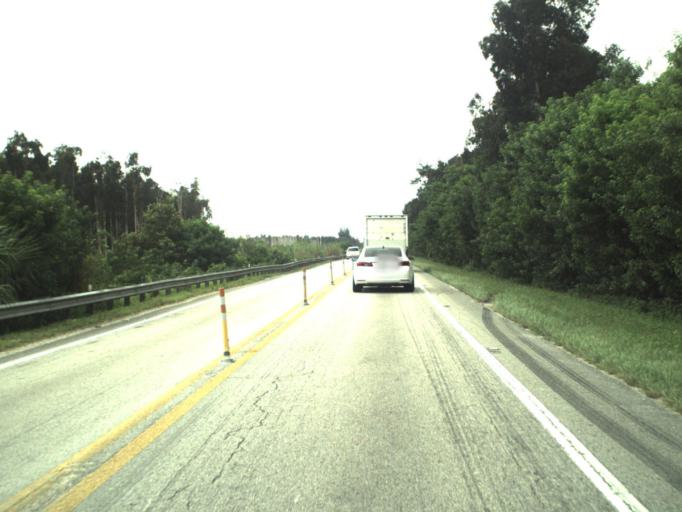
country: US
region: Florida
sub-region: Miami-Dade County
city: Kendall West
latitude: 25.7344
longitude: -80.4804
